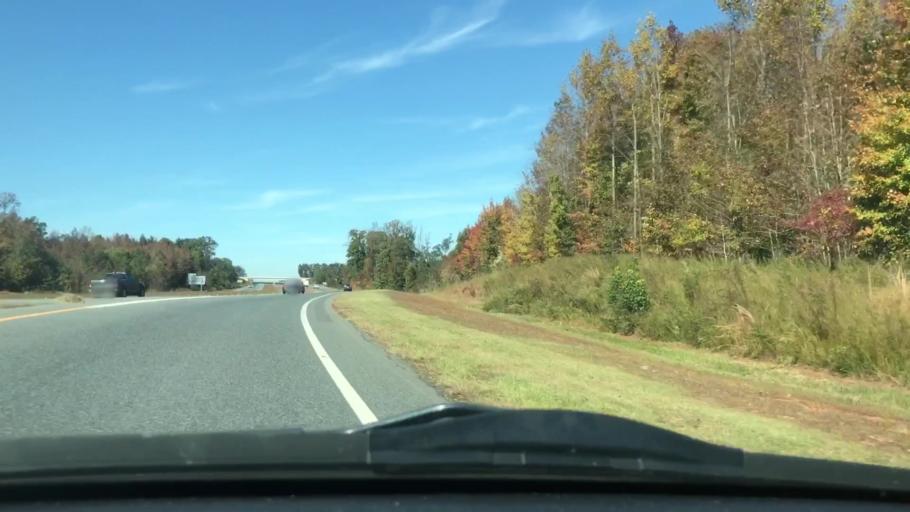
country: US
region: North Carolina
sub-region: Randolph County
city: Randleman
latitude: 35.8247
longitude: -79.8550
